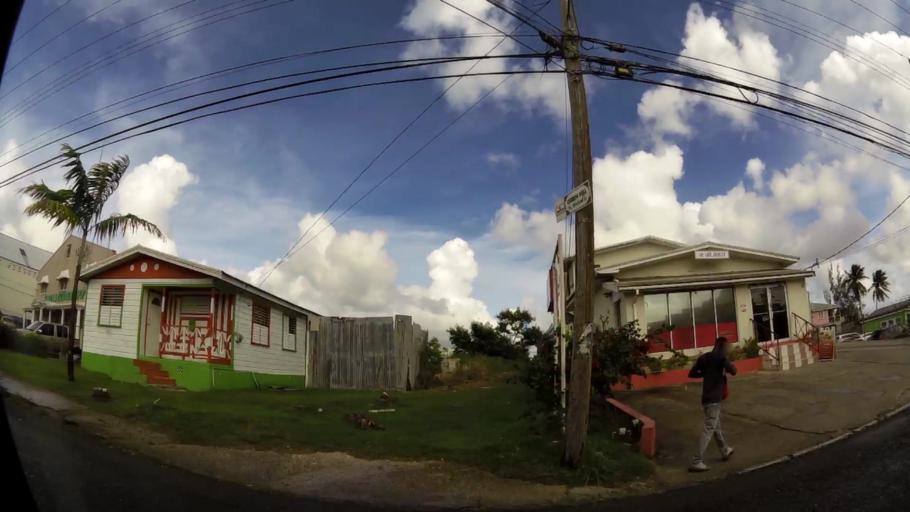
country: BB
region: Saint Michael
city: Bridgetown
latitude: 13.1347
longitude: -59.6058
